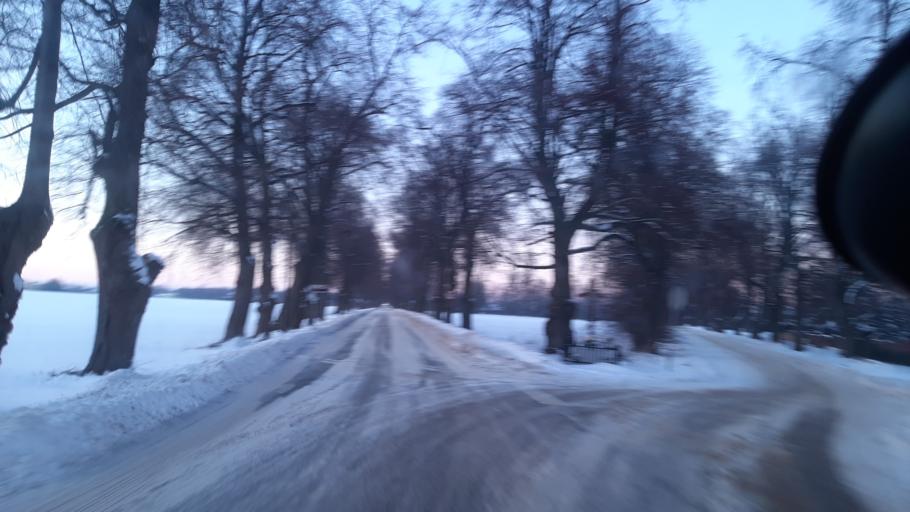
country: PL
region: Lublin Voivodeship
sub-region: Powiat lubelski
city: Lublin
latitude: 51.3252
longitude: 22.5605
